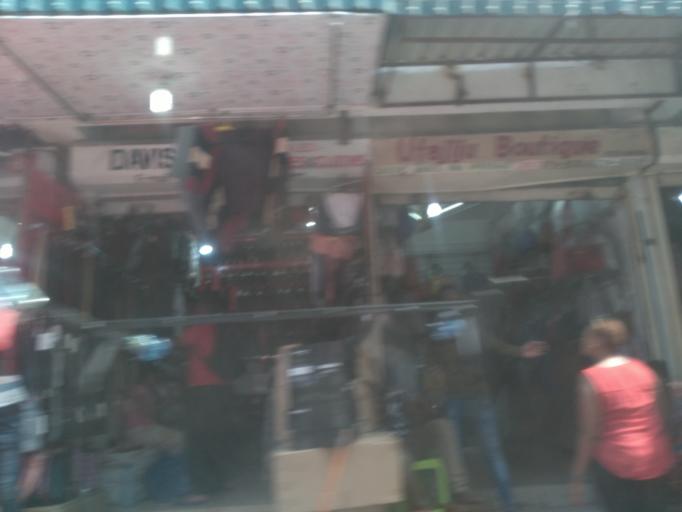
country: TZ
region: Dar es Salaam
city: Dar es Salaam
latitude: -6.8207
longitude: 39.2752
